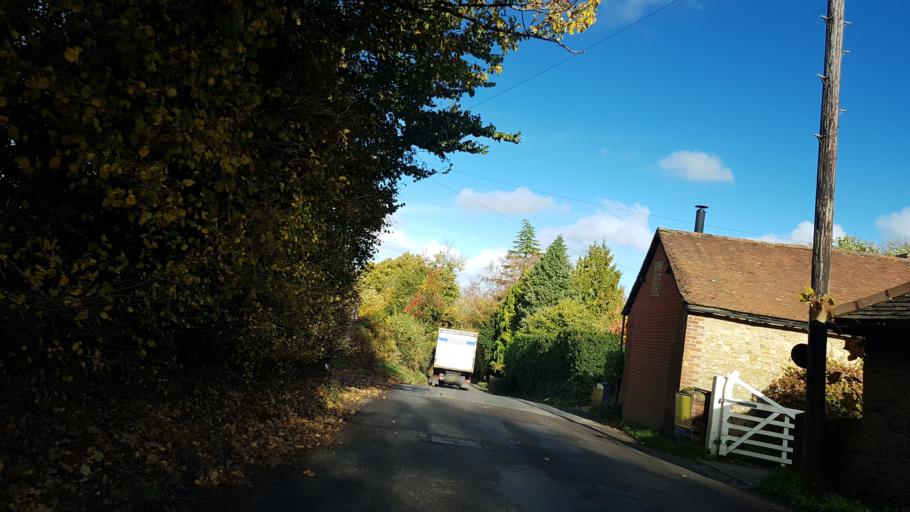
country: GB
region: England
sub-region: Surrey
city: Churt
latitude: 51.1362
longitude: -0.7505
